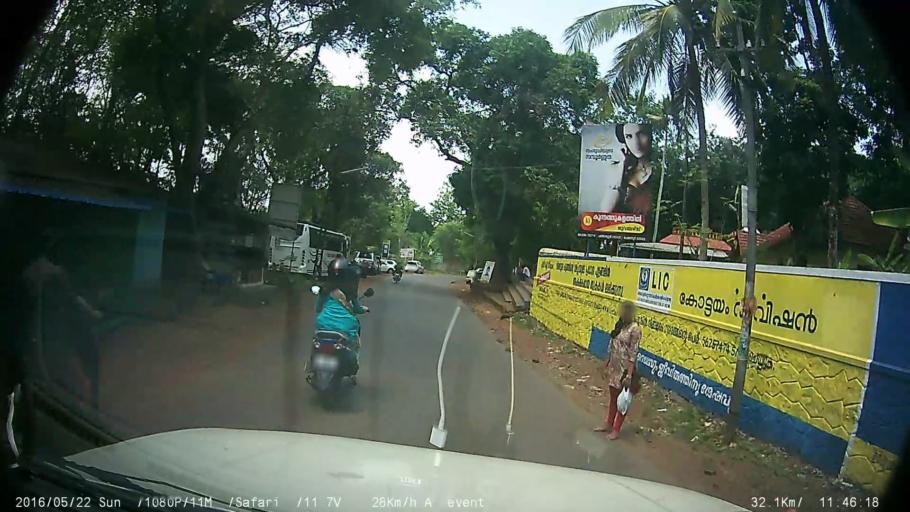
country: IN
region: Kerala
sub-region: Kottayam
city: Kottayam
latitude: 9.5351
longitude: 76.5222
